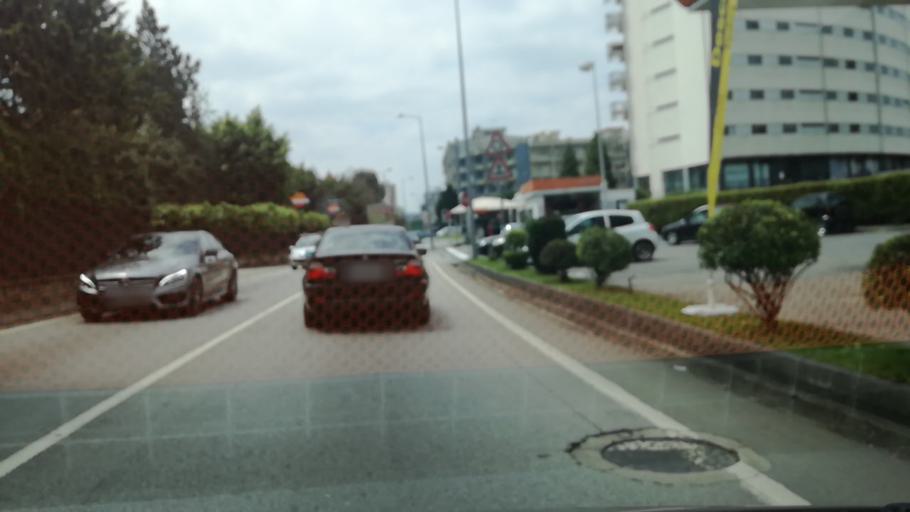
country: PT
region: Porto
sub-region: Trofa
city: Bougado
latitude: 41.3433
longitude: -8.5567
